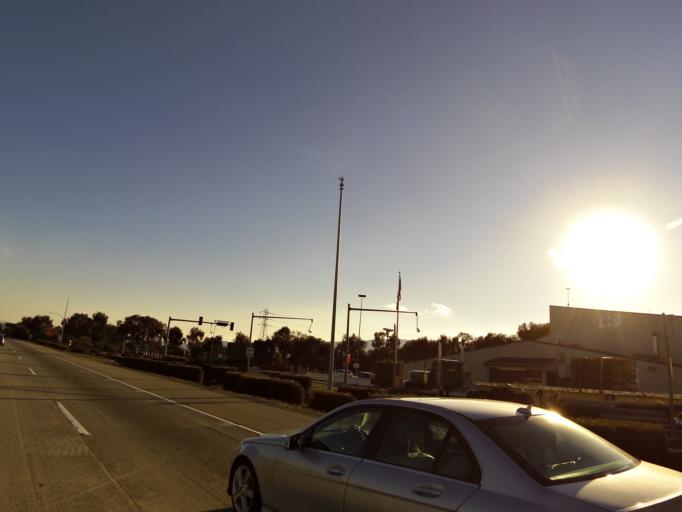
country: US
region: California
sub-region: Santa Clara County
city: Gilroy
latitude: 37.0406
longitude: -121.5766
